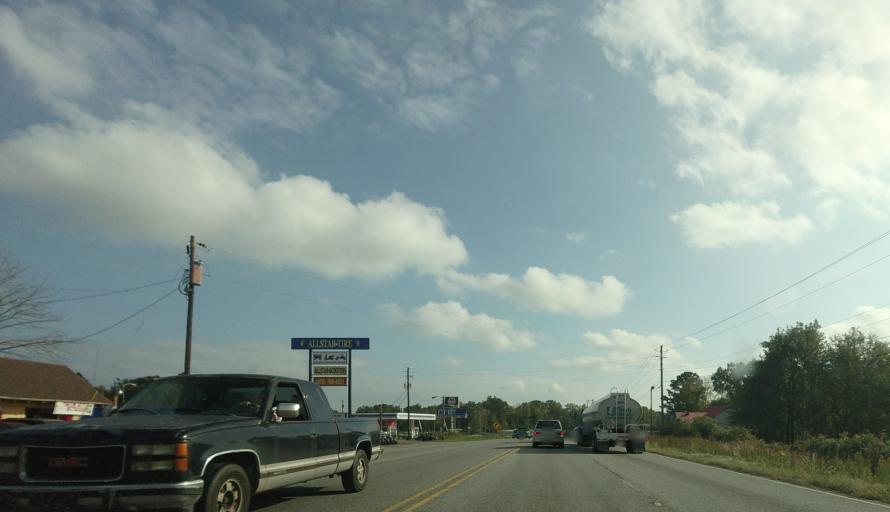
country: US
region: Georgia
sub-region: Bibb County
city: Macon
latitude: 32.7741
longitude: -83.6603
